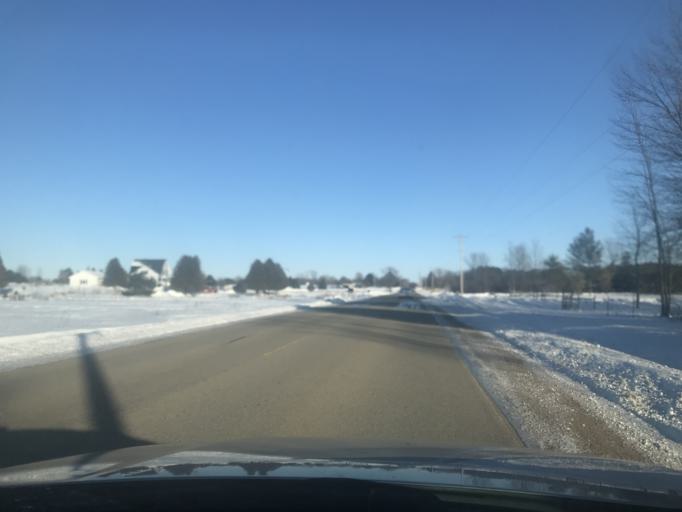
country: US
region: Wisconsin
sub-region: Marinette County
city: Marinette
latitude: 45.1449
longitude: -87.6623
